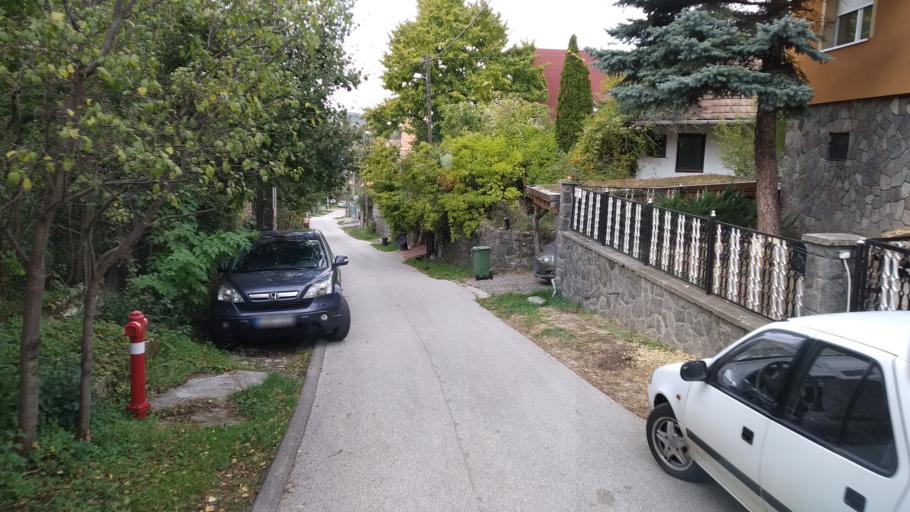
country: HU
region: Pest
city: Visegrad
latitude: 47.7220
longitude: 18.9922
